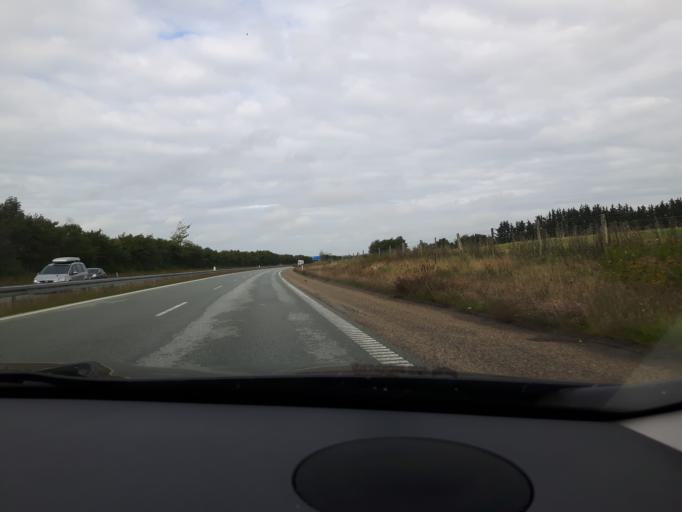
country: DK
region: North Denmark
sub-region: Hjorring Kommune
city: Hjorring
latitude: 57.4962
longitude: 10.0122
